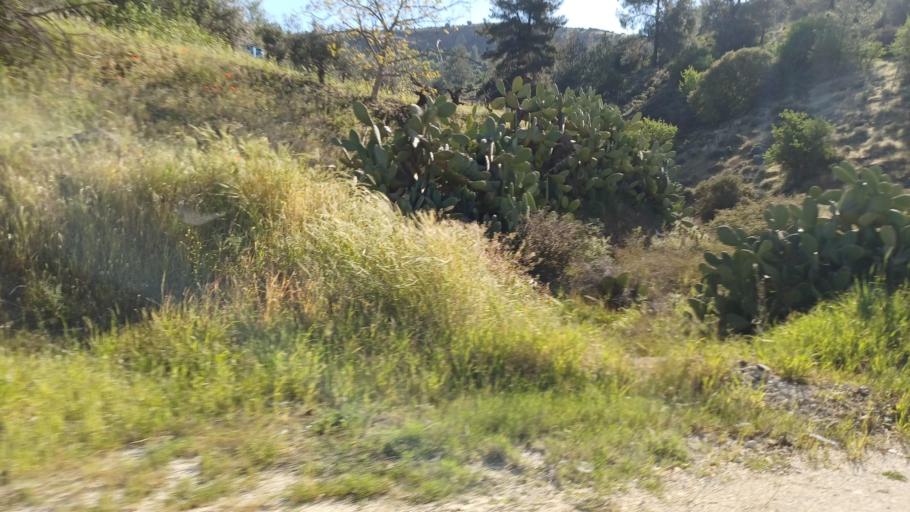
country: CY
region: Lefkosia
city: Peristerona
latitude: 35.0259
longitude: 33.0460
